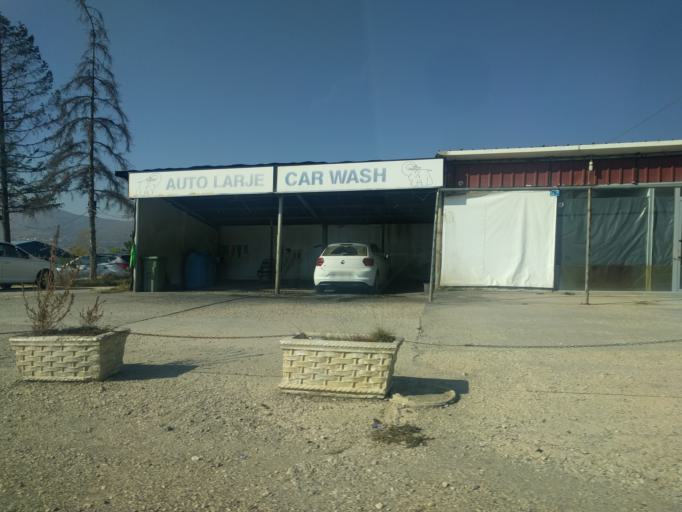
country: XK
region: Pristina
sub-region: Komuna e Gracanices
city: Glanica
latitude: 42.5929
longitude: 21.0187
